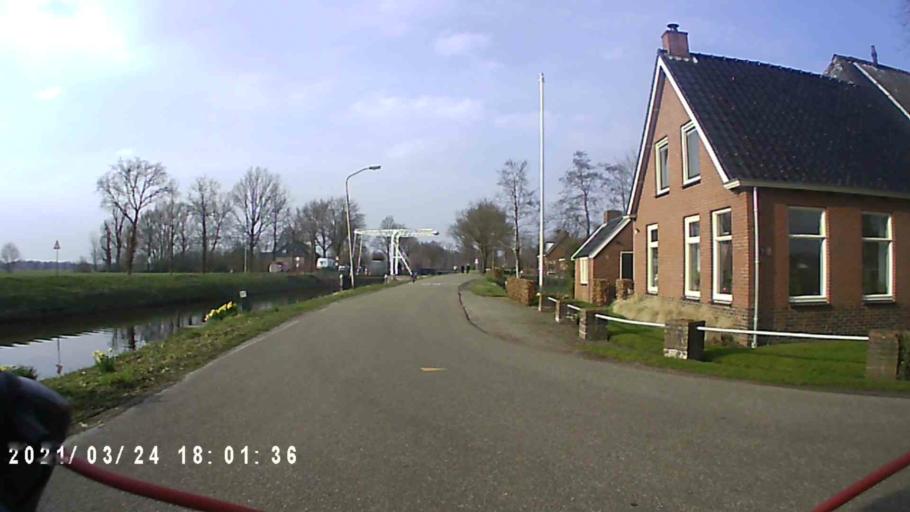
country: NL
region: Groningen
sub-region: Gemeente Leek
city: Leek
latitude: 53.1372
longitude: 6.3612
